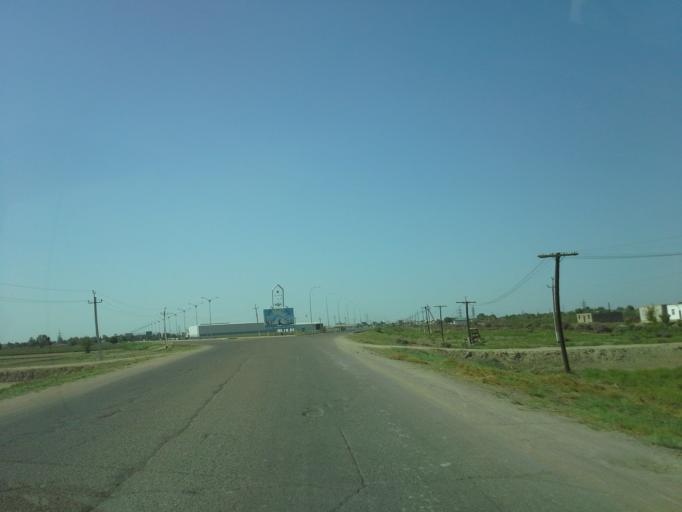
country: TM
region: Dasoguz
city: Dasoguz
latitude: 41.8076
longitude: 60.0047
